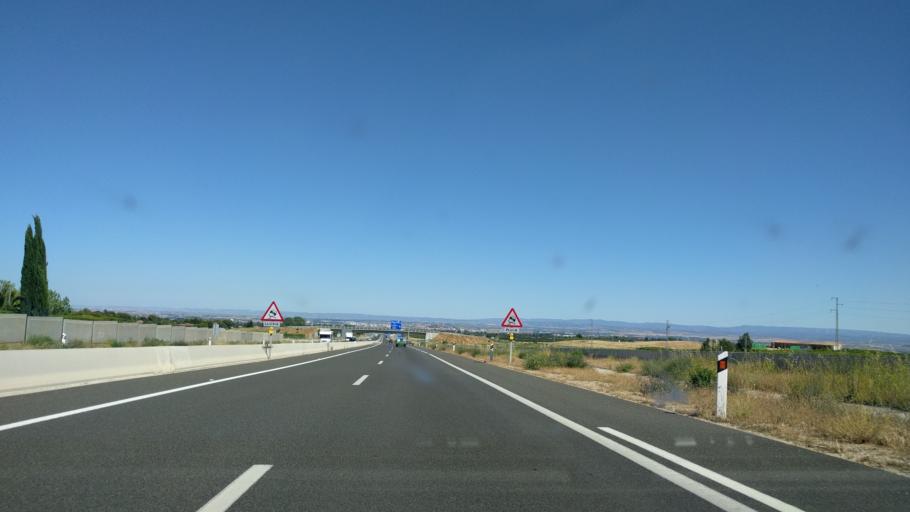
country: ES
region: Catalonia
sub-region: Provincia de Lleida
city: Alpicat
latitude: 41.6566
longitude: 0.5375
